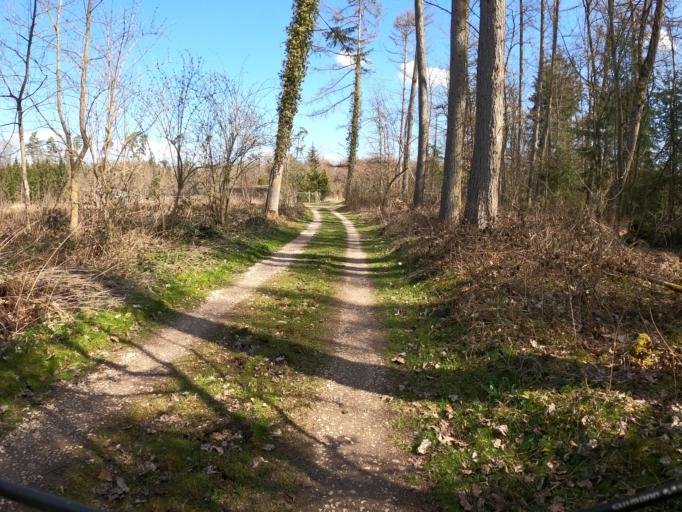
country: DE
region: Bavaria
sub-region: Swabia
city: Nersingen
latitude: 48.4007
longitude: 10.1497
